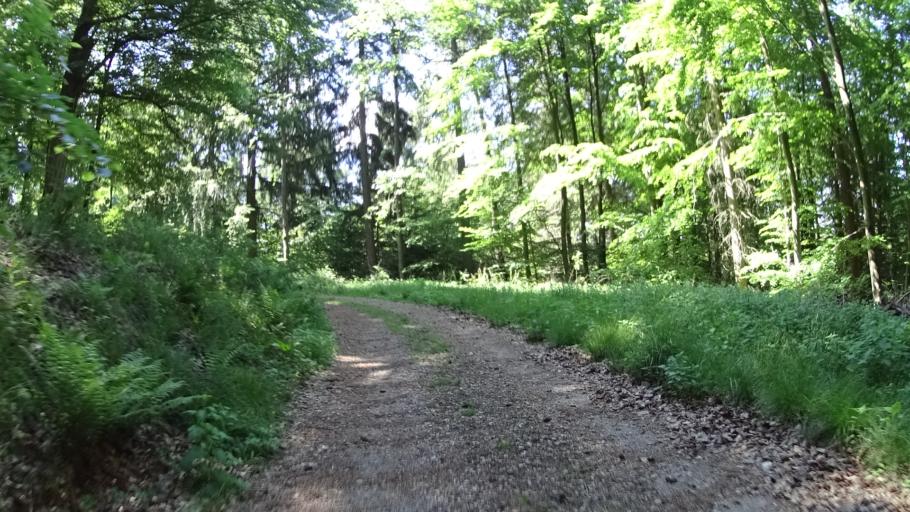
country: DE
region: Baden-Wuerttemberg
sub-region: Karlsruhe Region
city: Wilhelmsfeld
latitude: 49.4769
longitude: 8.7436
